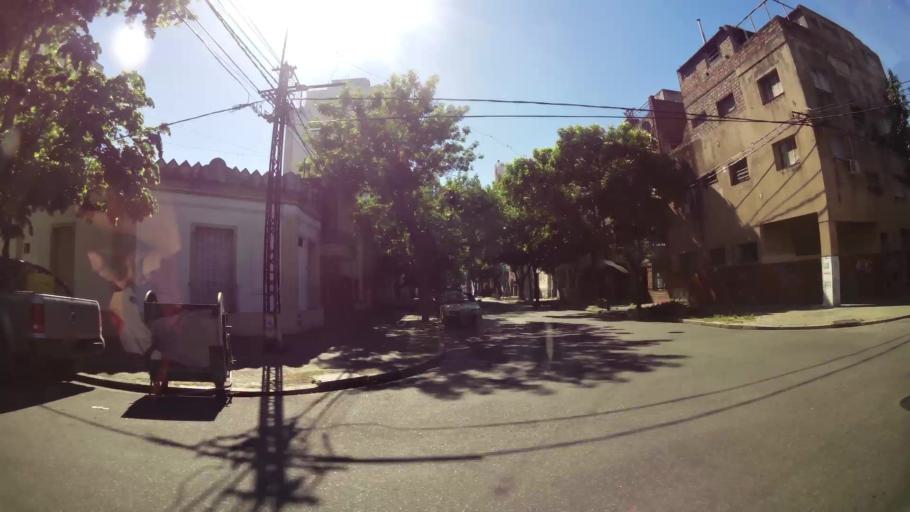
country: AR
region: Santa Fe
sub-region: Departamento de Rosario
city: Rosario
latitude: -32.9414
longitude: -60.6726
